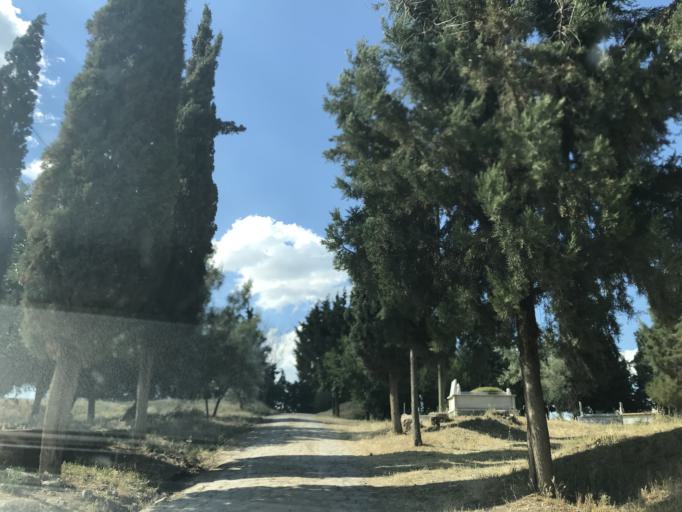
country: TR
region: Denizli
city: Civril
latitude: 38.3051
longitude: 29.7430
